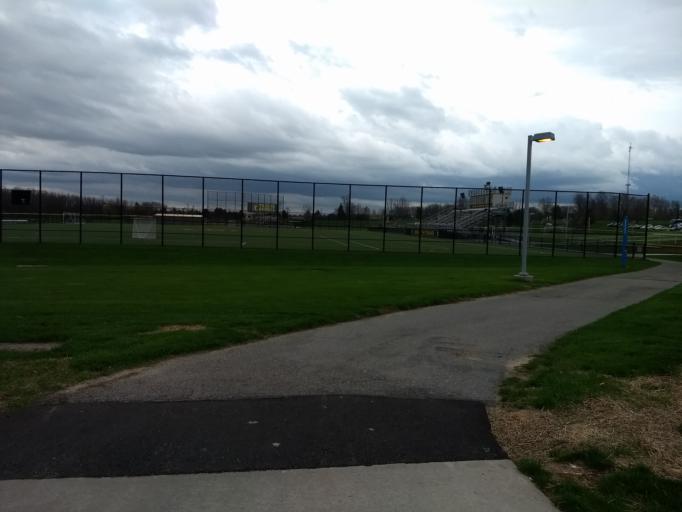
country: US
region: New York
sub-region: Monroe County
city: Rochester
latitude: 43.0996
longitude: -77.6078
